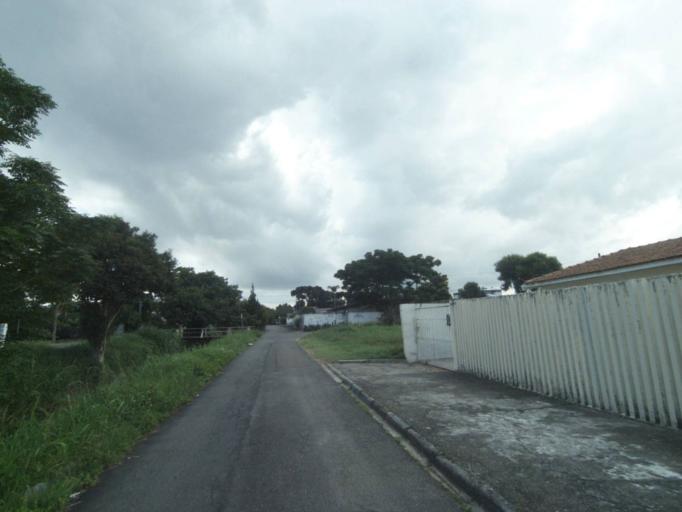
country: BR
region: Parana
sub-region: Pinhais
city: Pinhais
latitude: -25.4445
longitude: -49.2048
